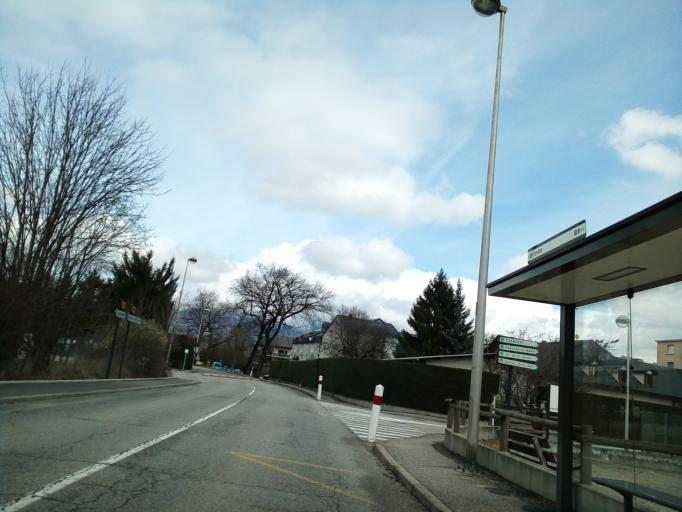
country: FR
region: Rhone-Alpes
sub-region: Departement de la Savoie
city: Saint-Baldoph
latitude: 45.5309
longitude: 5.9560
